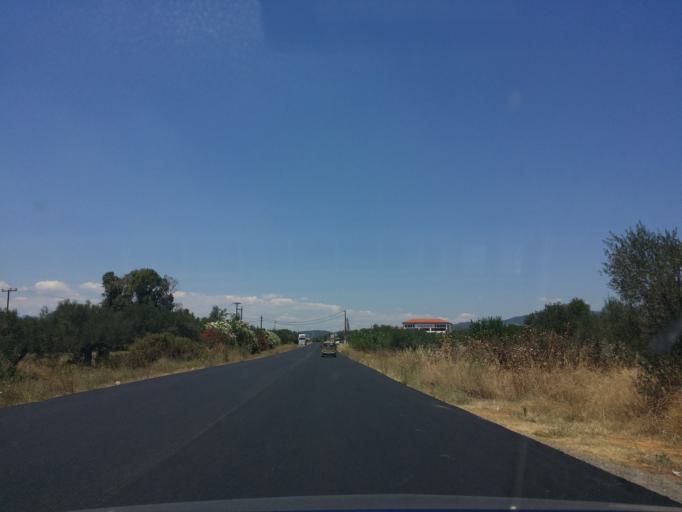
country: GR
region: Peloponnese
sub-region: Nomos Lakonias
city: Sparti
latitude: 37.0819
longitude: 22.4466
